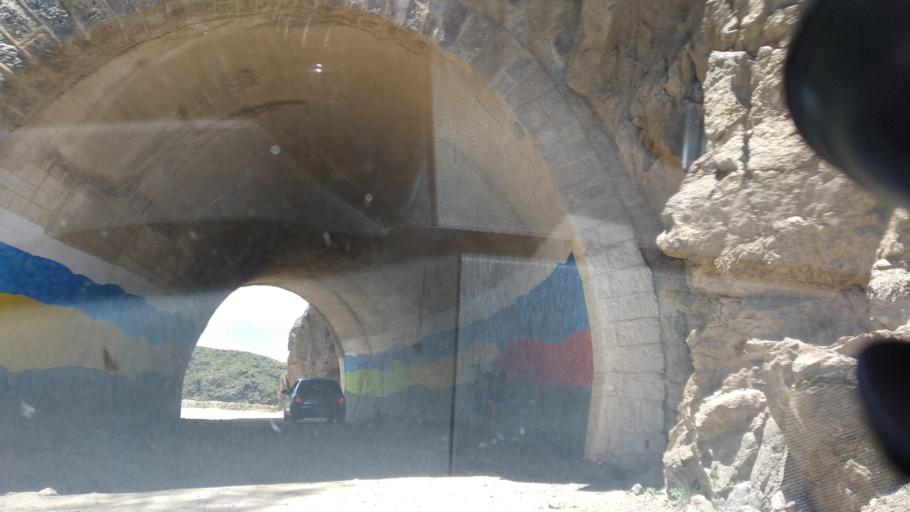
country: AR
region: Cordoba
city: Salsacate
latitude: -31.3778
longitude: -65.4070
